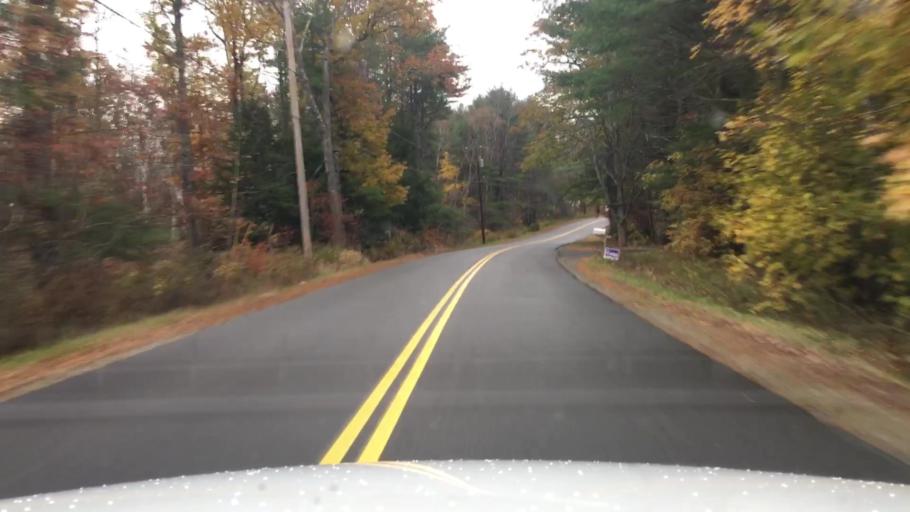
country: US
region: Maine
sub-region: Kennebec County
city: Pittston
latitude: 44.1716
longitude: -69.7304
